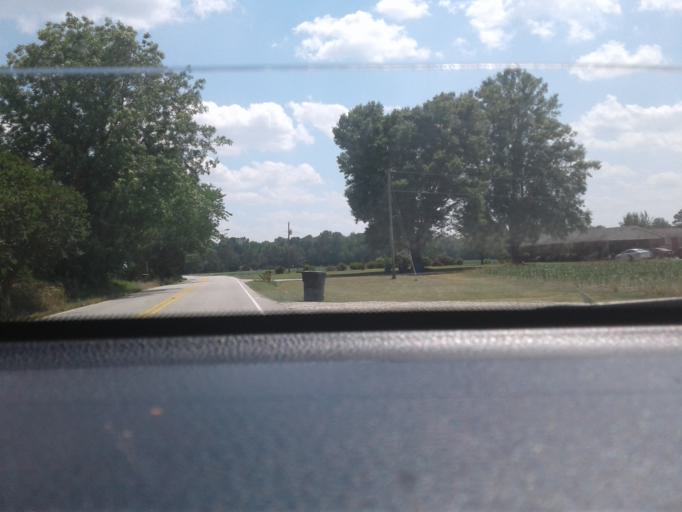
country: US
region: North Carolina
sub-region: Harnett County
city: Erwin
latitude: 35.2795
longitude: -78.6721
